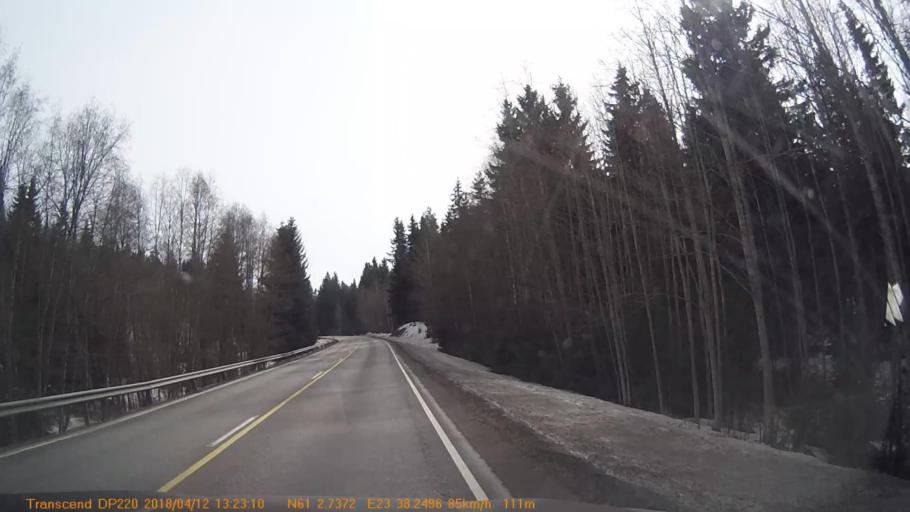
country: FI
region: Pirkanmaa
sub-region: Etelae-Pirkanmaa
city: Urjala
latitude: 61.0446
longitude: 23.6386
